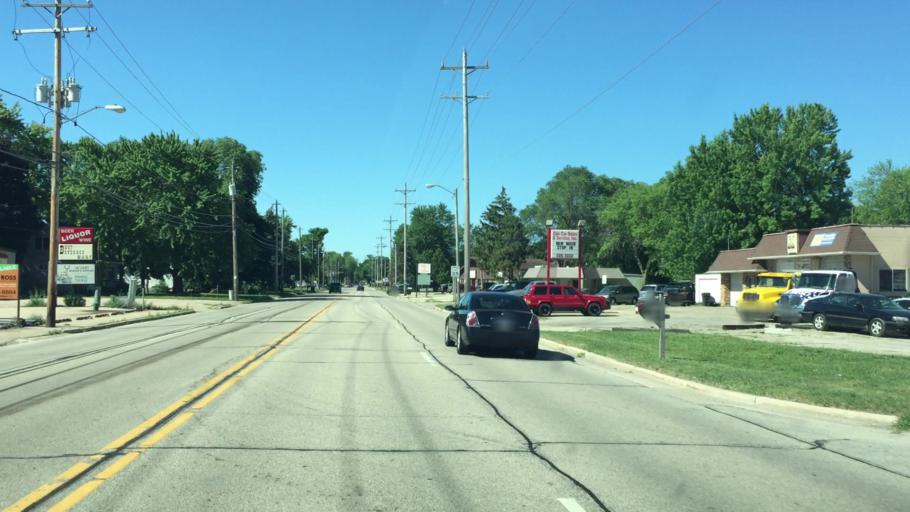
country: US
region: Wisconsin
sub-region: Winnebago County
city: Menasha
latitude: 44.2188
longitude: -88.4305
